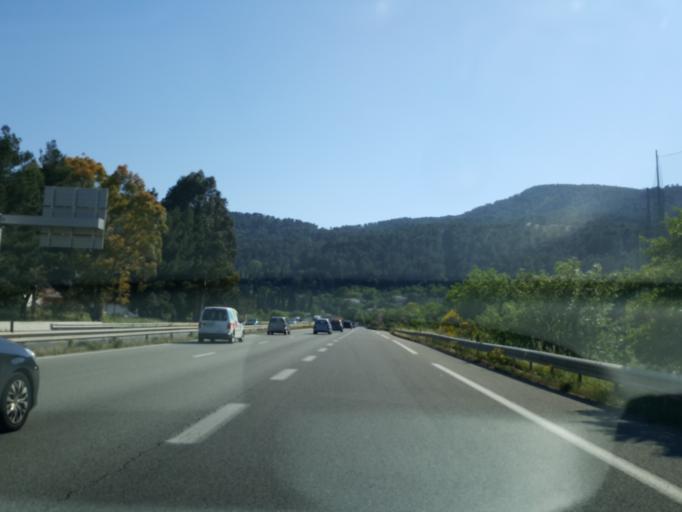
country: FR
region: Provence-Alpes-Cote d'Azur
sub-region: Departement du Var
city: Sollies-Pont
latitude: 43.1942
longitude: 6.0393
